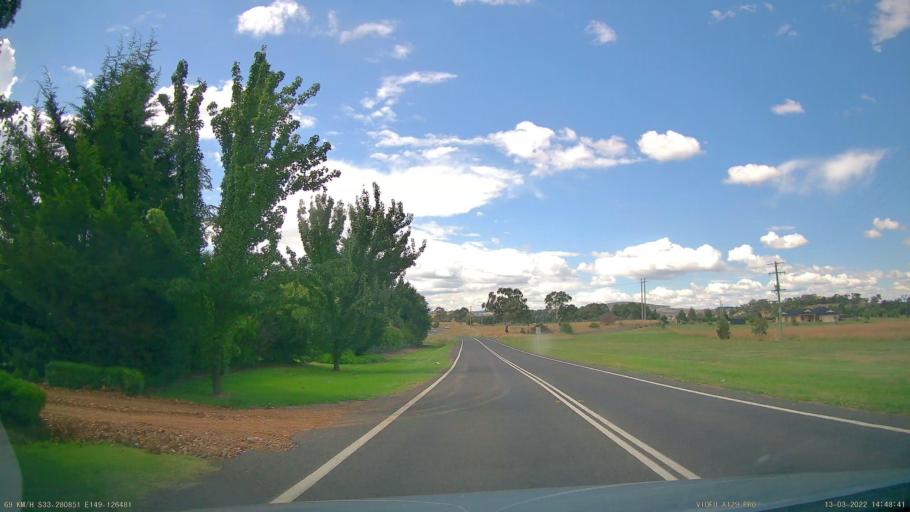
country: AU
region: New South Wales
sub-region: Orange Municipality
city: Orange
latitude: -33.2807
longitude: 149.1267
